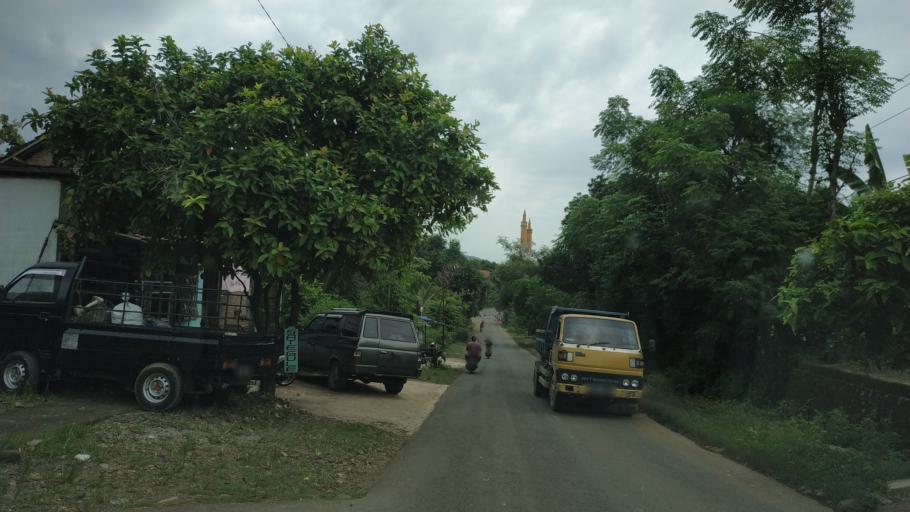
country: ID
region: Central Java
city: Krajan Tegalombo
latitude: -6.4457
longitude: 110.9865
